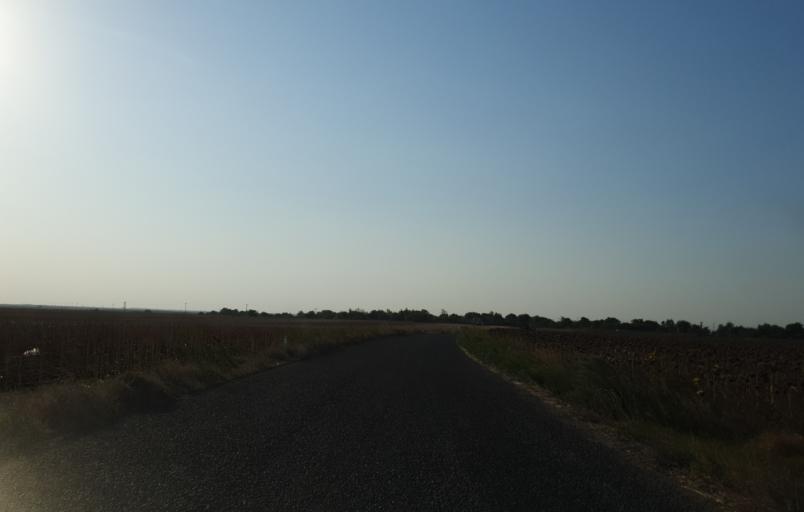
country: TR
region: Tekirdag
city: Beyazkoy
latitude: 41.4287
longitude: 27.7591
